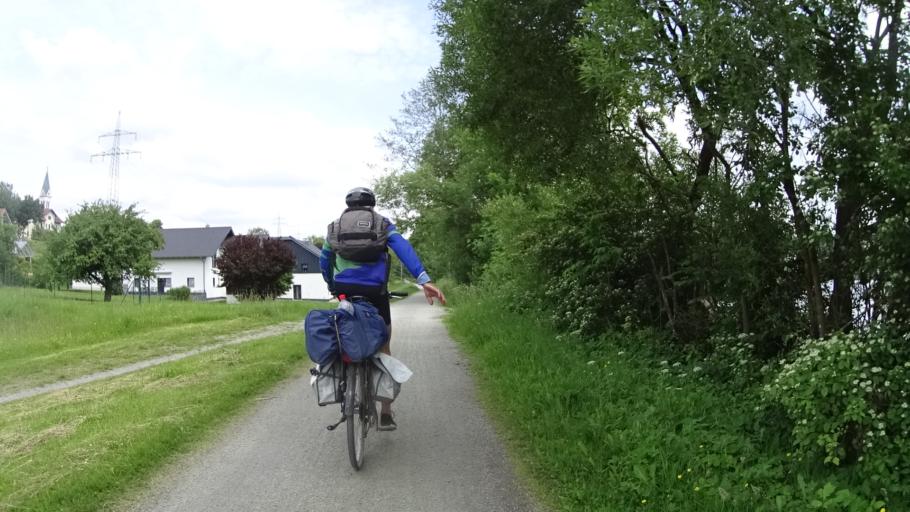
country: DE
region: Bavaria
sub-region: Lower Bavaria
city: Tiefenbach
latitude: 48.6012
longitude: 13.3603
